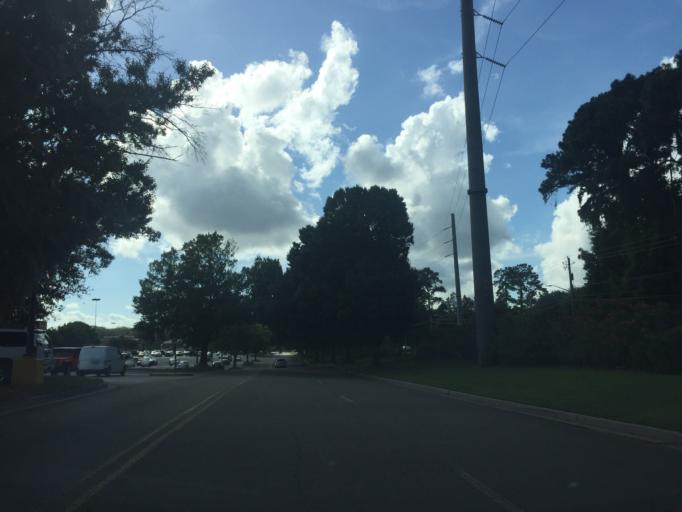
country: US
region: Georgia
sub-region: Chatham County
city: Georgetown
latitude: 31.9849
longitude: -81.1697
